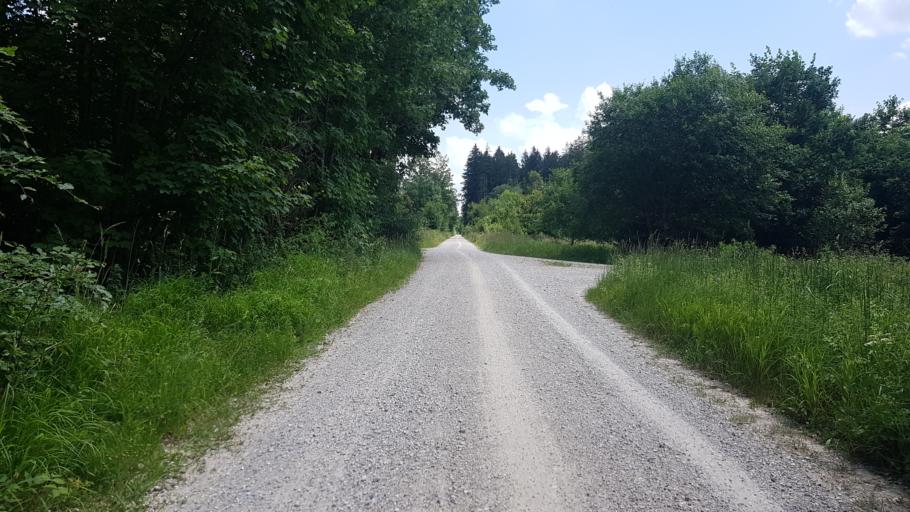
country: DE
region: Bavaria
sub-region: Upper Bavaria
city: Planegg
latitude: 48.0512
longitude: 11.4284
